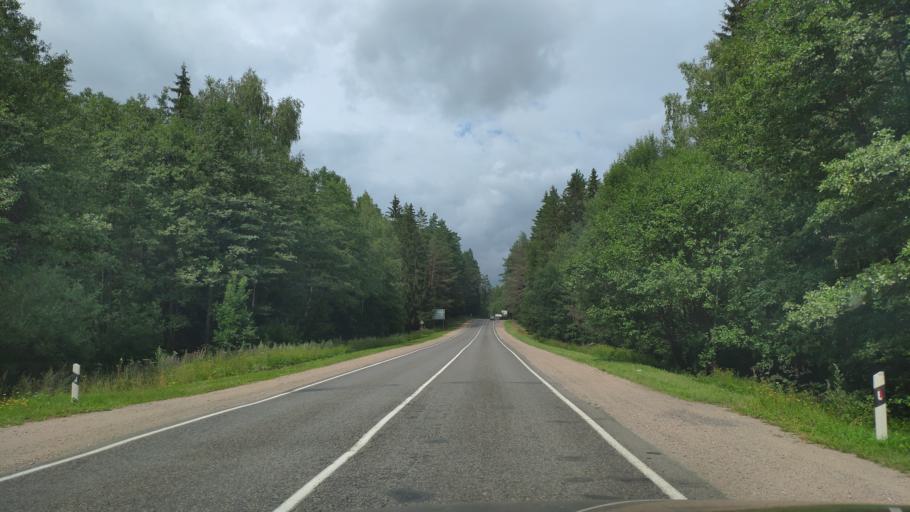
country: BY
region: Minsk
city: Zaslawye
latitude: 53.9747
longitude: 27.2488
